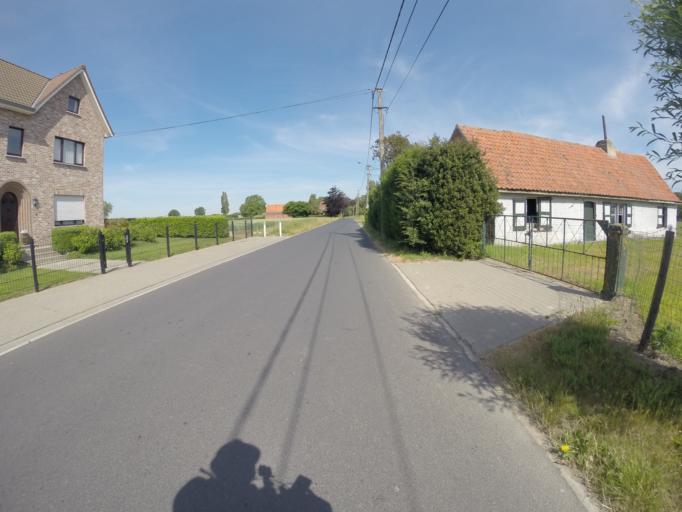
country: BE
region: Flanders
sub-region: Provincie Oost-Vlaanderen
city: Knesselare
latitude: 51.1720
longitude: 3.3825
